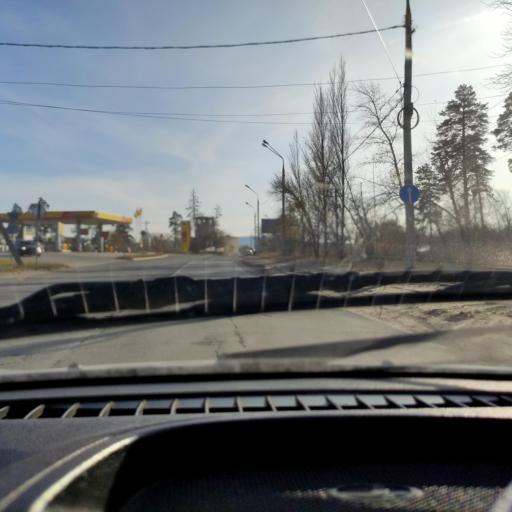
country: RU
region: Samara
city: Zhigulevsk
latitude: 53.4683
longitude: 49.5477
